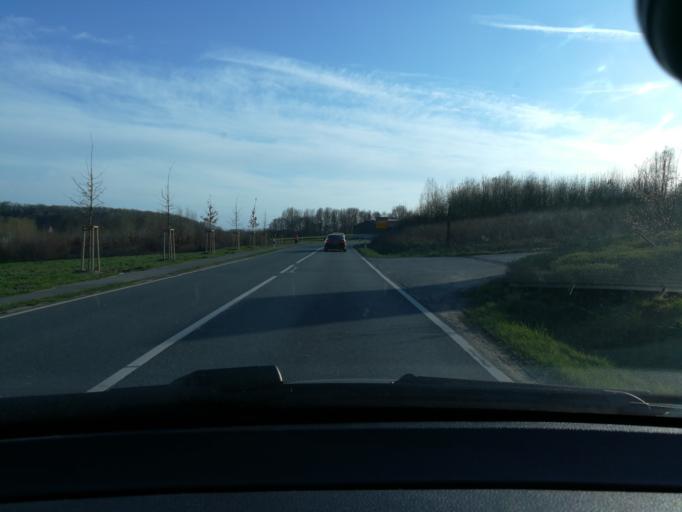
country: DE
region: North Rhine-Westphalia
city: Borgholzhausen
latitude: 52.0936
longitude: 8.2898
